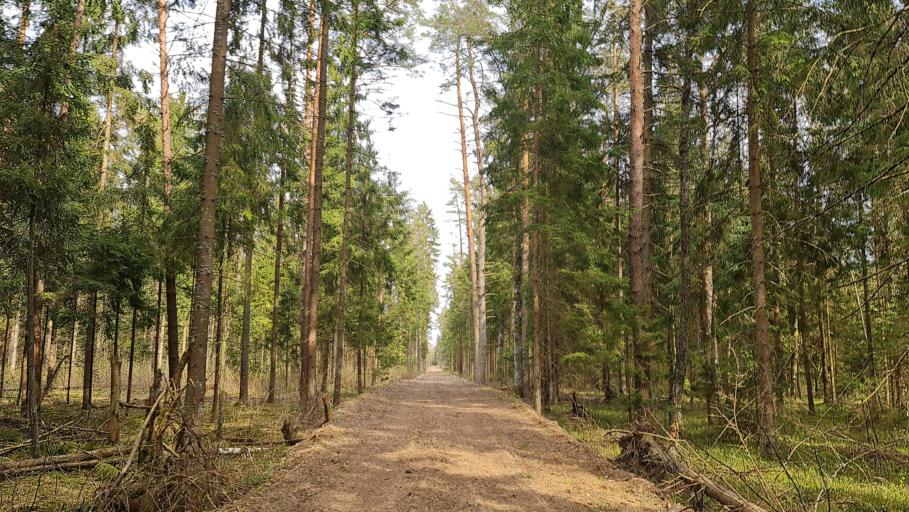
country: BY
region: Vitebsk
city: Byahoml'
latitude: 54.7496
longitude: 28.0426
